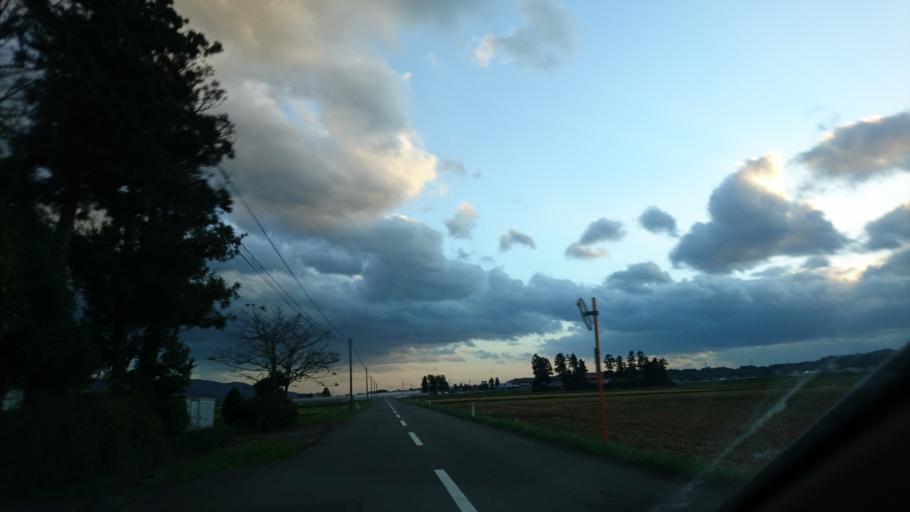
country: JP
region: Iwate
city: Mizusawa
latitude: 39.1090
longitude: 141.1501
